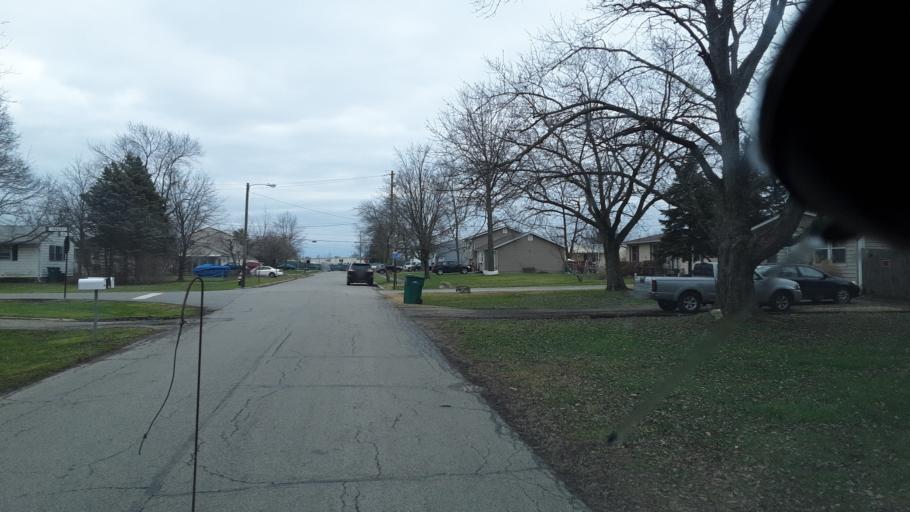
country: US
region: Ohio
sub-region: Franklin County
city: Obetz
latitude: 39.8772
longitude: -82.9400
